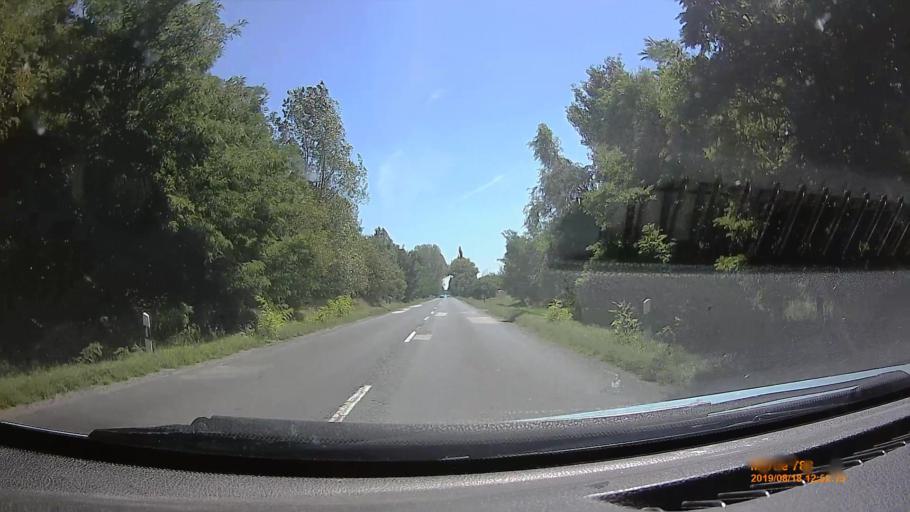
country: HU
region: Fejer
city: Aba
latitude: 47.0647
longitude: 18.5151
